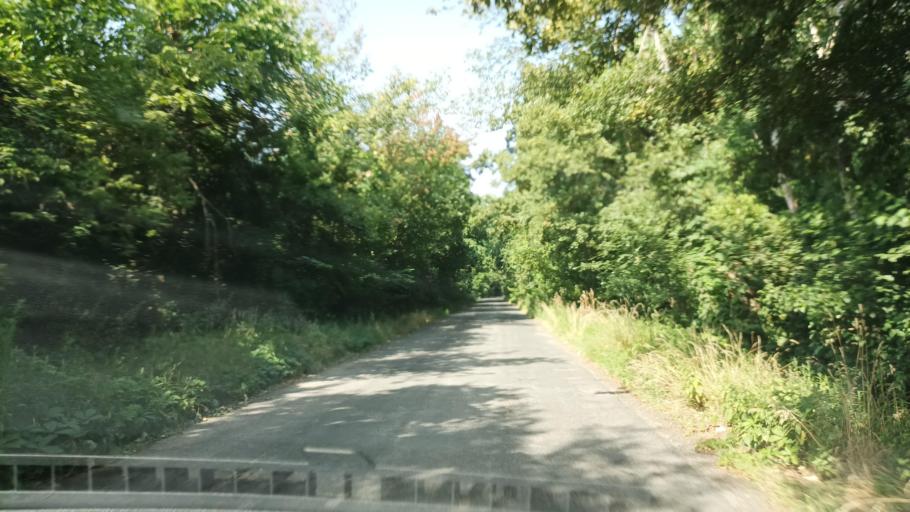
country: HU
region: Pest
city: Szigetujfalu
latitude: 47.2357
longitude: 18.9191
